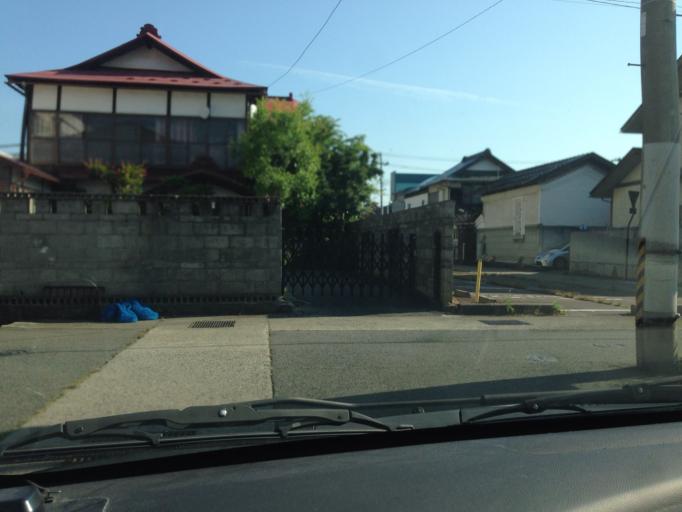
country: JP
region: Fukushima
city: Kitakata
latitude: 37.5604
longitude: 139.8230
